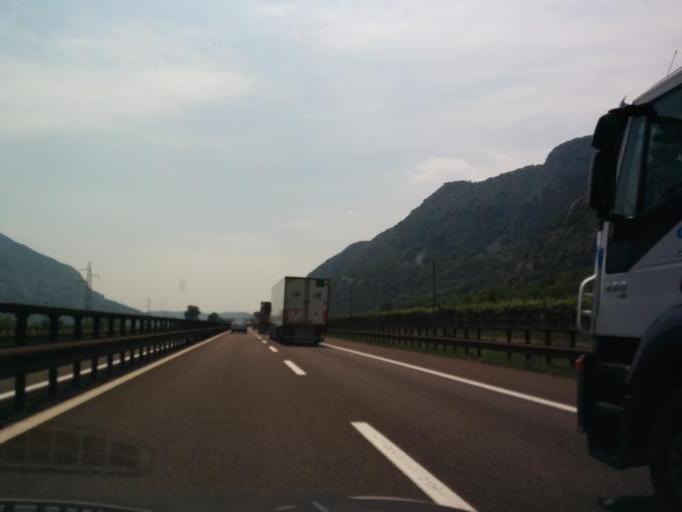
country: IT
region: Veneto
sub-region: Provincia di Verona
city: Dolce
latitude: 45.6028
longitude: 10.8460
